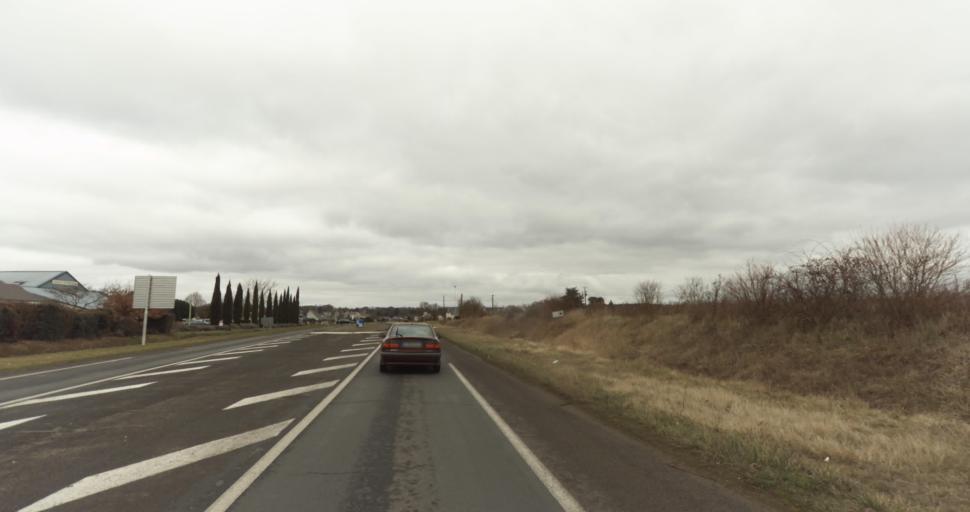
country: FR
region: Pays de la Loire
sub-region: Departement de Maine-et-Loire
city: Varrains
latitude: 47.2158
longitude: -0.0595
